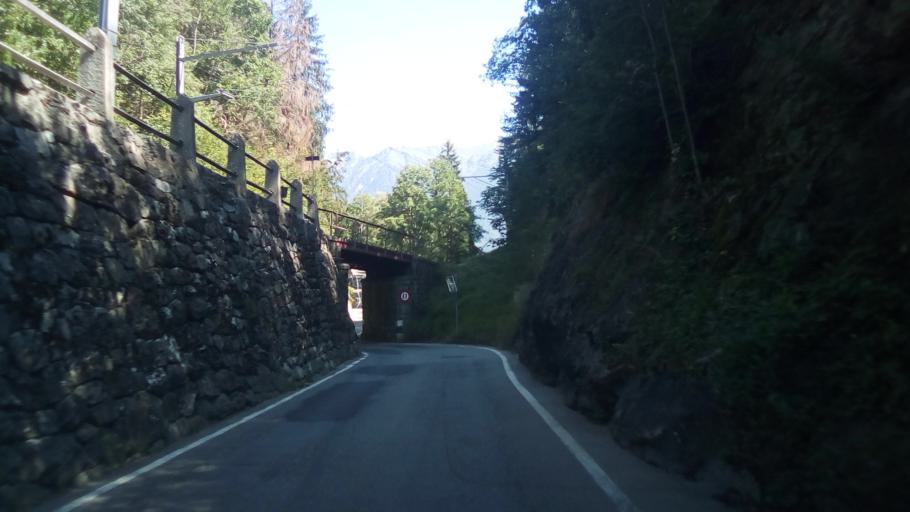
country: CH
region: Valais
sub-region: Saint-Maurice District
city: Salvan
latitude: 46.1221
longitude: 7.0221
